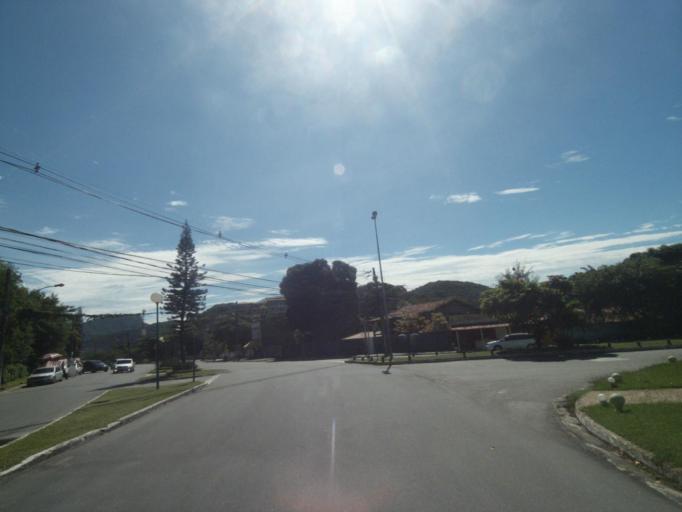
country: BR
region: Rio de Janeiro
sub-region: Niteroi
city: Niteroi
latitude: -22.9518
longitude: -43.0586
